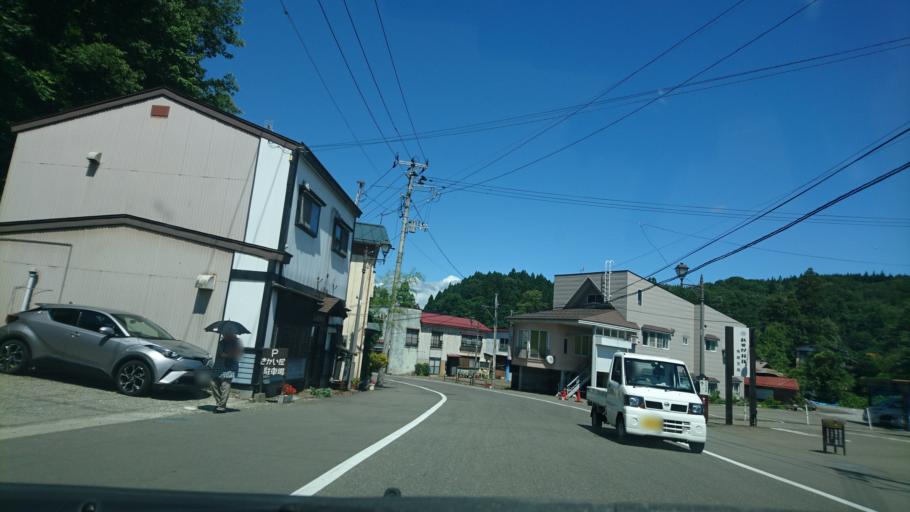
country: JP
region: Akita
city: Kakunodatemachi
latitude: 39.5933
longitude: 140.5683
